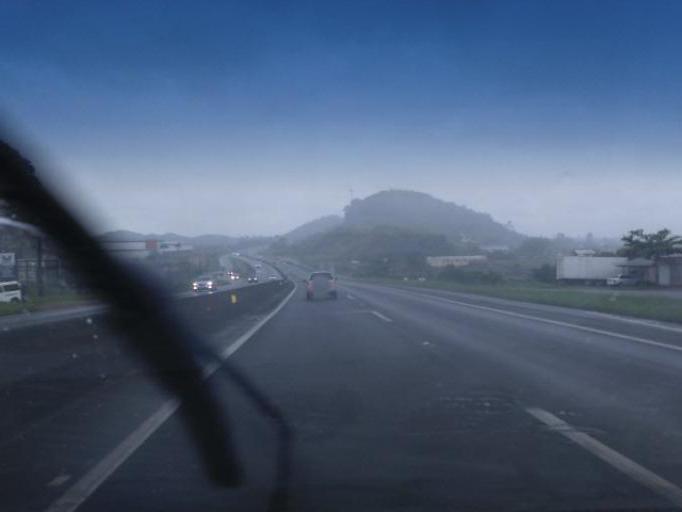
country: BR
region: Santa Catarina
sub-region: Penha
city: Penha
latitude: -26.7185
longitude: -48.7022
